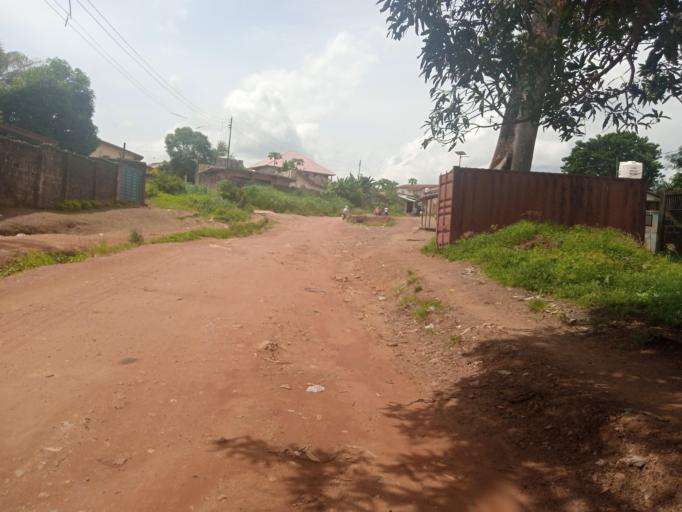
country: SL
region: Southern Province
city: Bo
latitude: 7.9656
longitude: -11.7426
